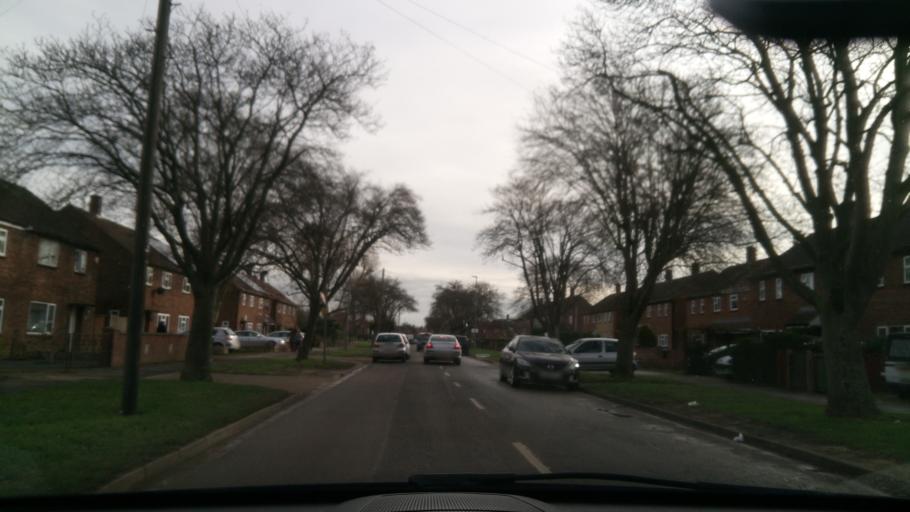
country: GB
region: England
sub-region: Peterborough
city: Peterborough
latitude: 52.5991
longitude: -0.2275
